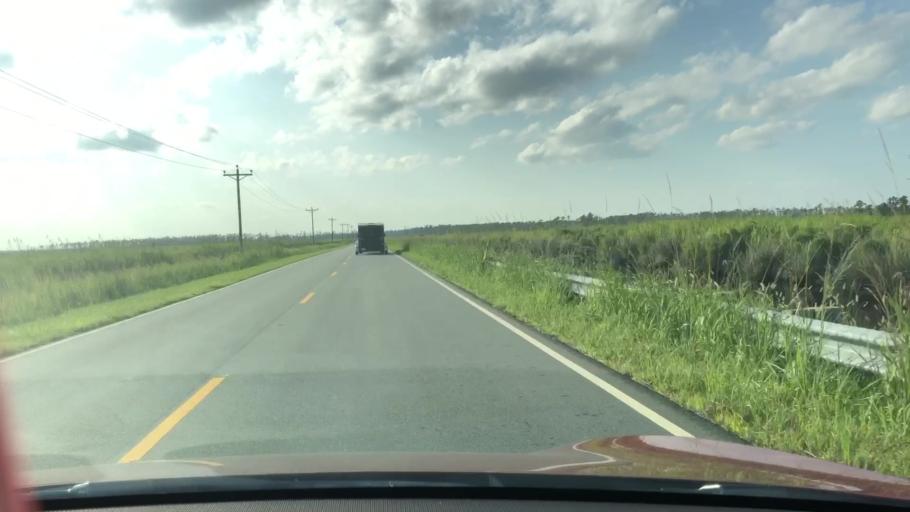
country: US
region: North Carolina
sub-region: Dare County
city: Wanchese
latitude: 35.6290
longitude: -75.8512
